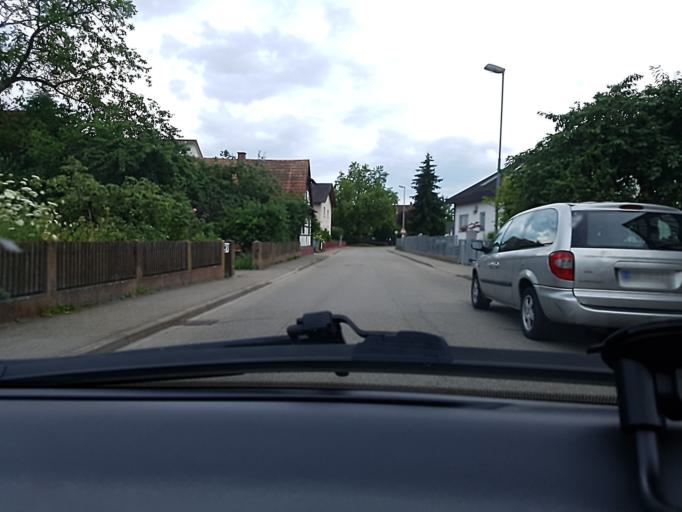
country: DE
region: Baden-Wuerttemberg
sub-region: Freiburg Region
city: Willstatt
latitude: 48.5677
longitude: 7.8720
